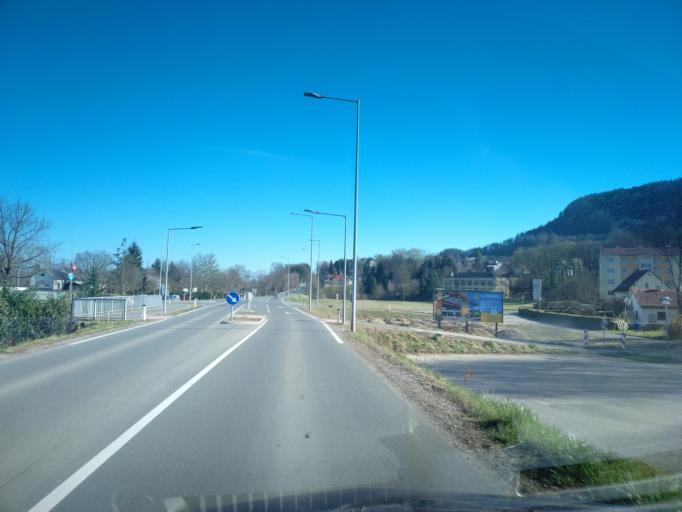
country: AT
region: Styria
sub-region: Politischer Bezirk Leibnitz
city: Wildon
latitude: 46.8840
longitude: 15.5197
